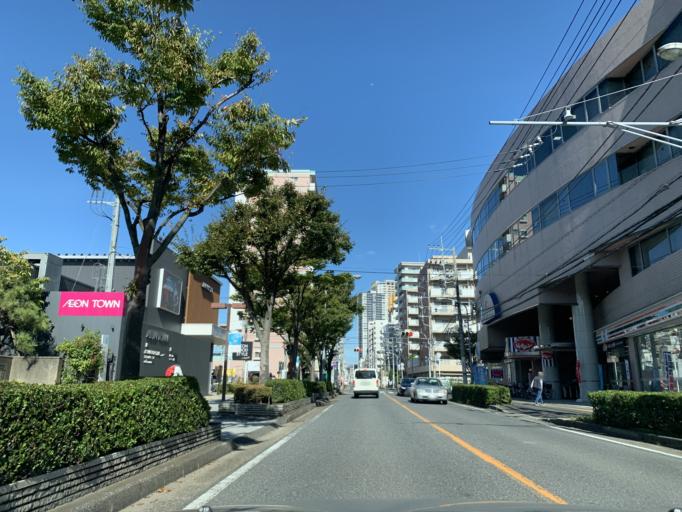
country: JP
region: Tokyo
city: Urayasu
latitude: 35.7173
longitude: 139.9224
